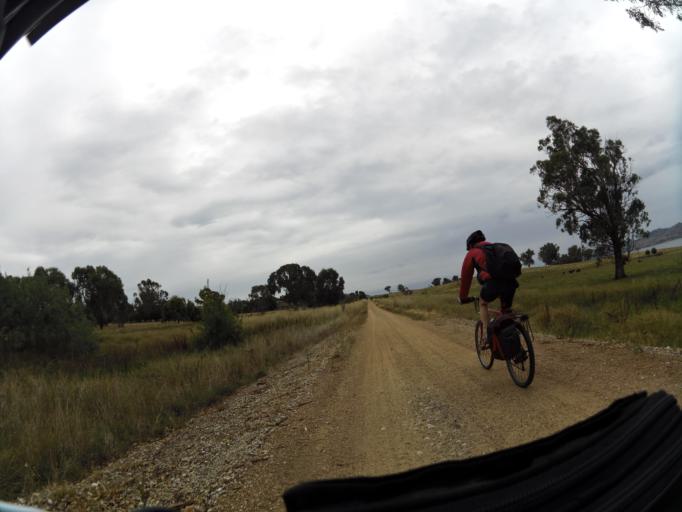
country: AU
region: New South Wales
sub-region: Albury Municipality
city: East Albury
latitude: -36.2094
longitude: 147.0538
